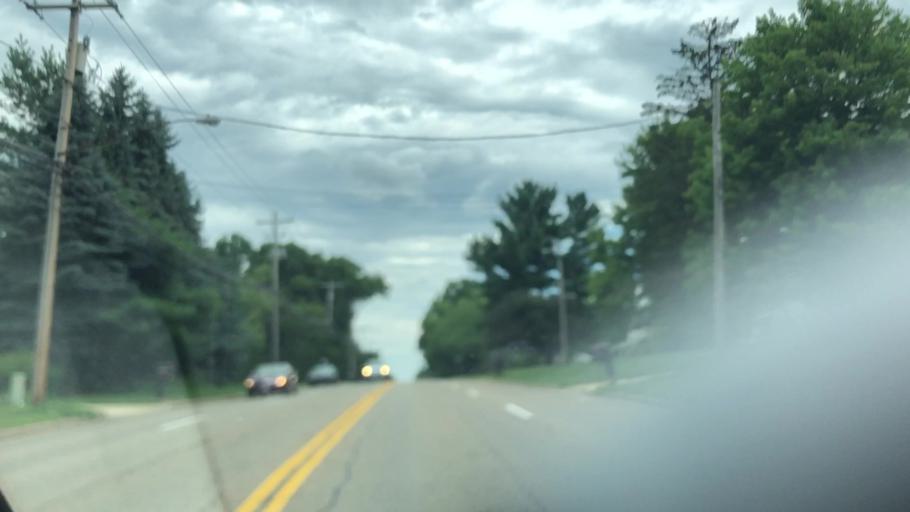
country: US
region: Ohio
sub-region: Summit County
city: Fairlawn
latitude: 41.1155
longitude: -81.6098
